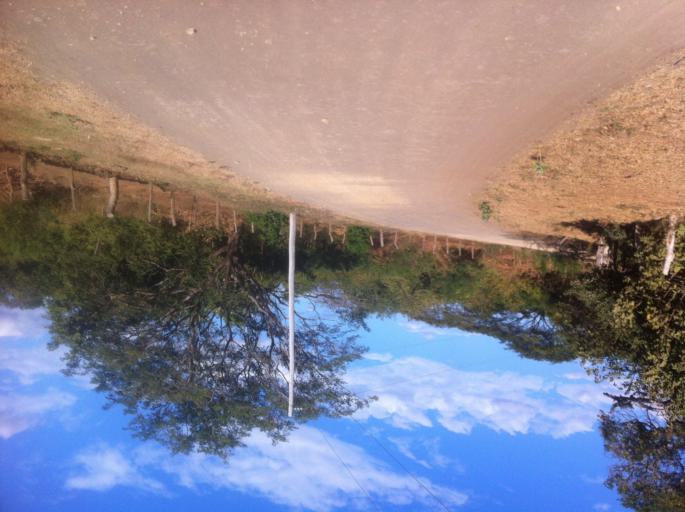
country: NI
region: Managua
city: Carlos Fonseca Amador
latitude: 11.9158
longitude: -86.6013
